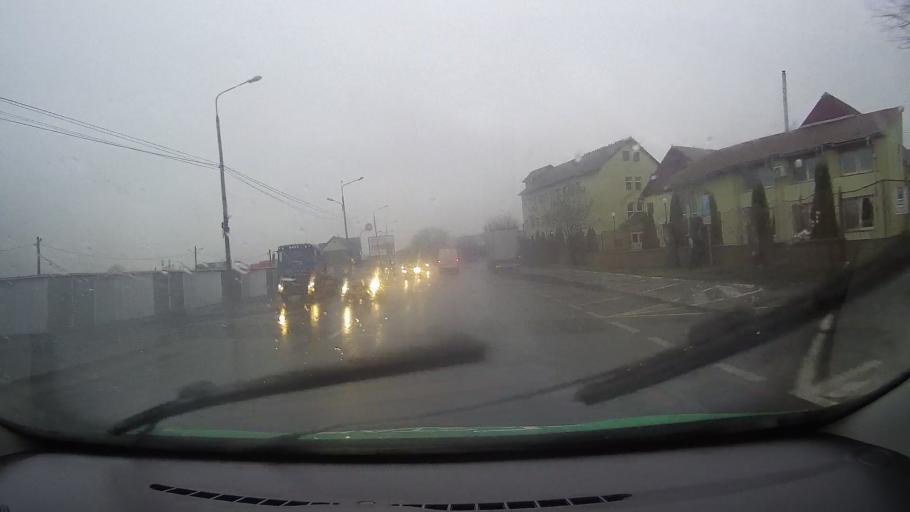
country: RO
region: Sibiu
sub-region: Municipiul Sibiu
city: Sibiu
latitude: 45.8164
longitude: 24.1494
